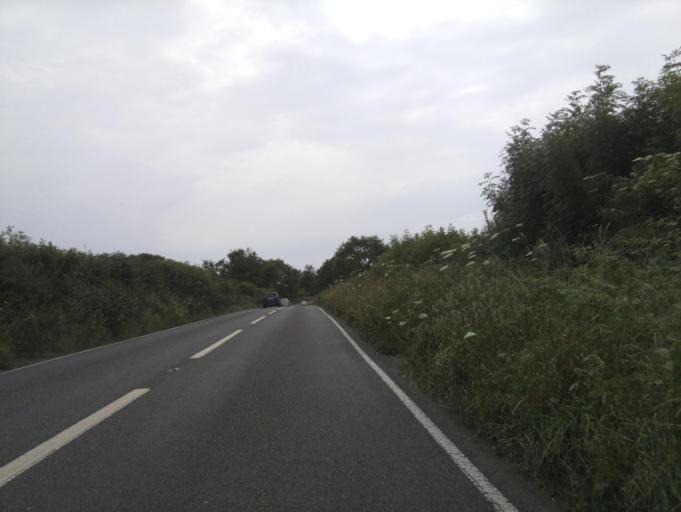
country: GB
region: England
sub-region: Devon
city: Sidmouth
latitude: 50.7034
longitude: -3.1846
